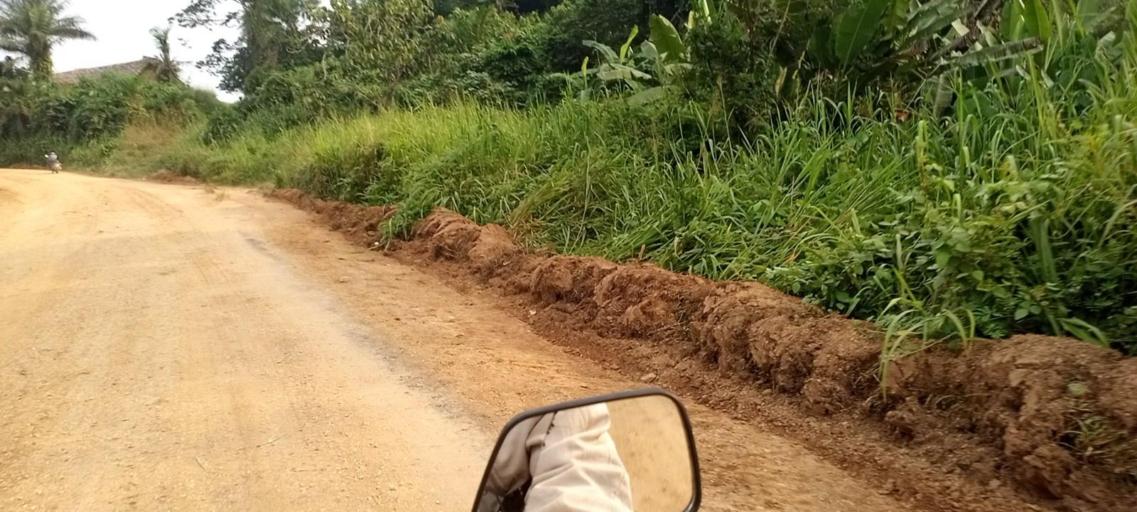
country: CD
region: Eastern Province
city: Kisangani
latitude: 0.1932
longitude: 25.5320
